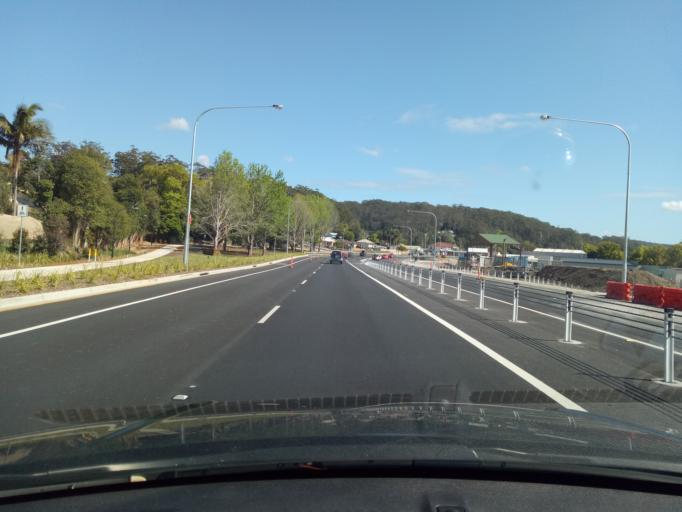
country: AU
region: New South Wales
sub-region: Gosford Shire
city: Lisarow
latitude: -33.3661
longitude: 151.3735
